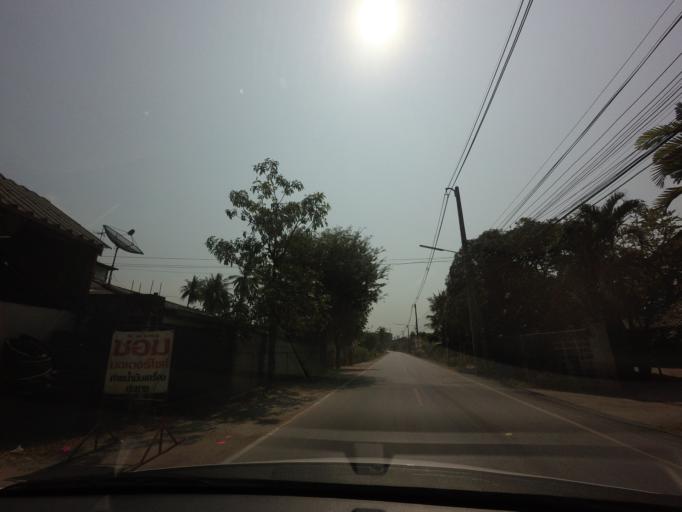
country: TH
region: Nakhon Pathom
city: Nakhon Chai Si
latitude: 13.7801
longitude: 100.2374
